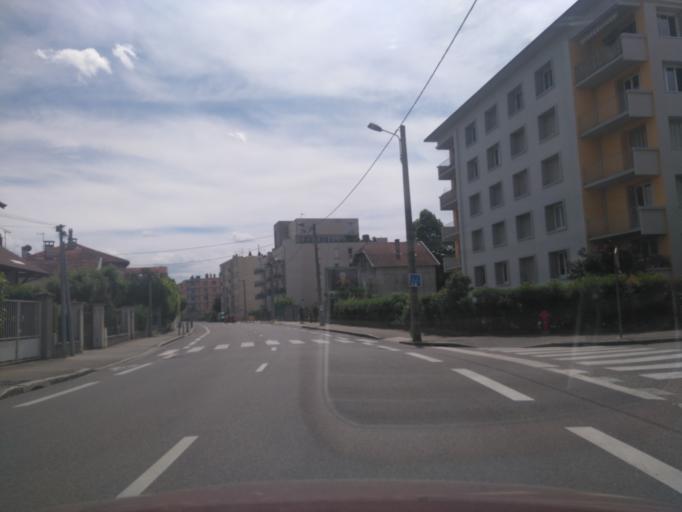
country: FR
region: Rhone-Alpes
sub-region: Departement de l'Isere
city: La Tronche
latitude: 45.1824
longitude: 5.7409
